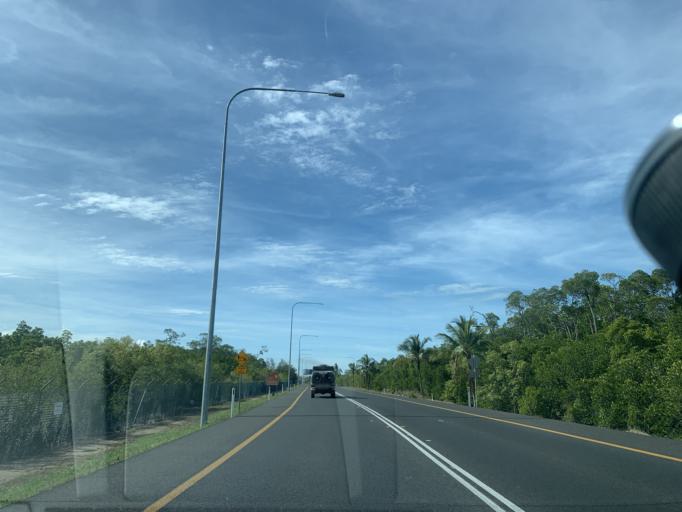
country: AU
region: Queensland
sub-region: Cairns
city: Cairns
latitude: -16.8863
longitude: 145.7622
